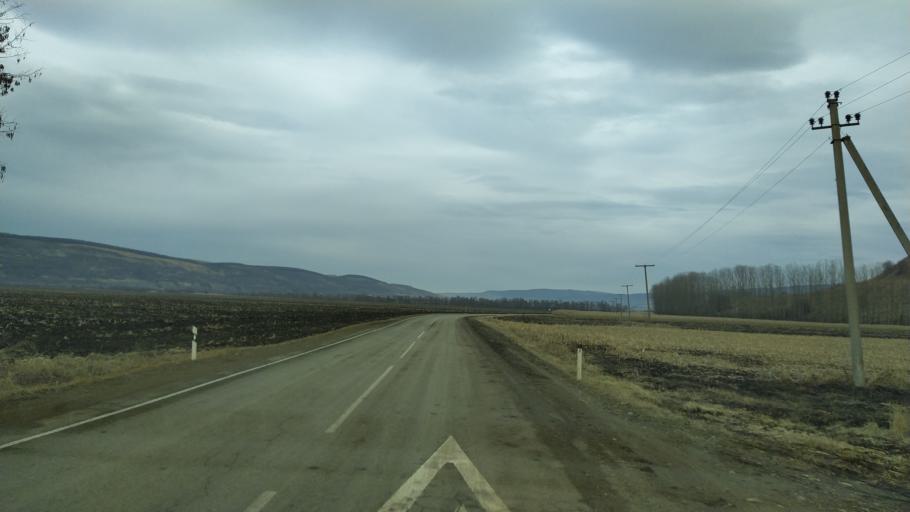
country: RU
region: Krasnodarskiy
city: Peredovaya
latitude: 44.1040
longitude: 41.4157
